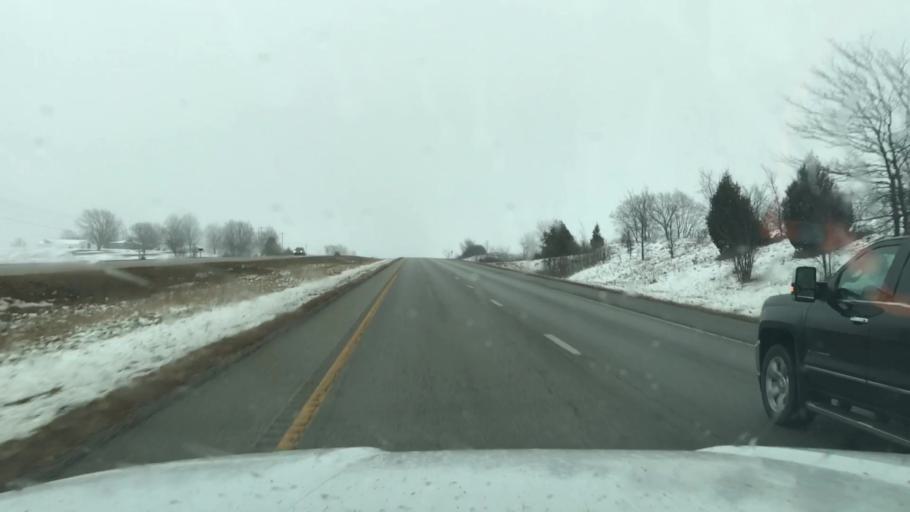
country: US
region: Missouri
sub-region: Clinton County
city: Gower
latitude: 39.7473
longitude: -94.6497
